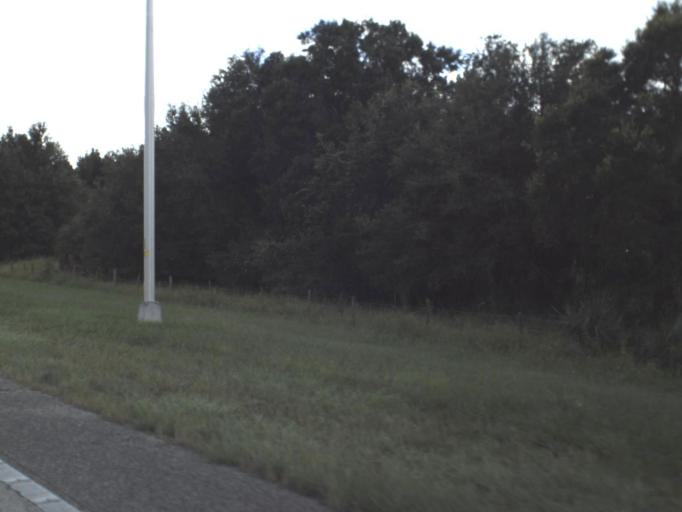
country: US
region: Florida
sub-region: Polk County
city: Fuller Heights
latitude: 27.9027
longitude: -82.0061
